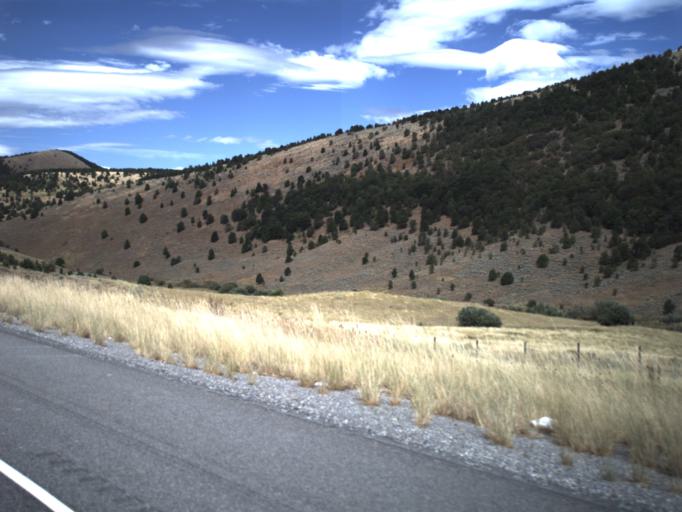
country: US
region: Utah
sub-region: Cache County
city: Wellsville
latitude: 41.5920
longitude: -111.9775
